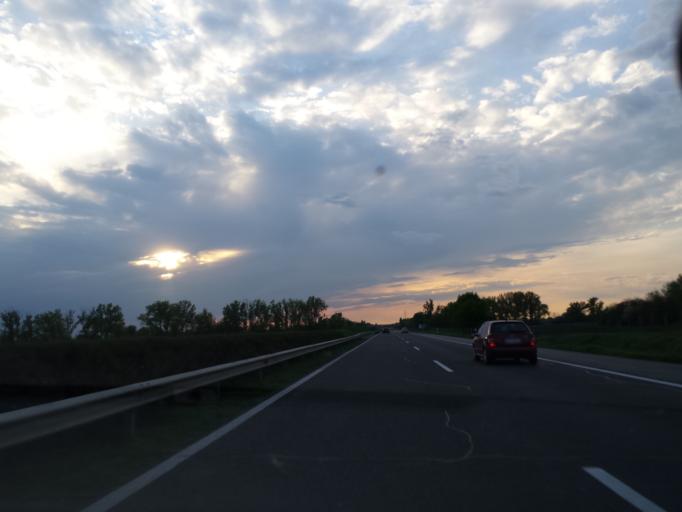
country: HU
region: Gyor-Moson-Sopron
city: Lebeny
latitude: 47.7680
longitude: 17.3803
